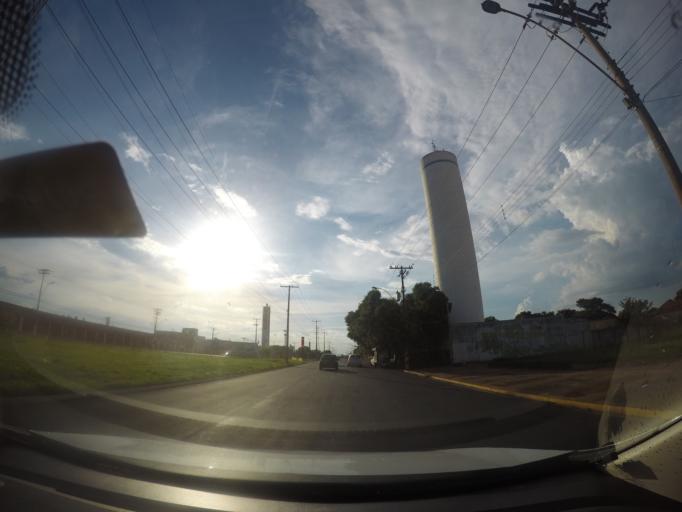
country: BR
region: Sao Paulo
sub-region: Matao
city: Matao
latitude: -21.6134
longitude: -48.3702
